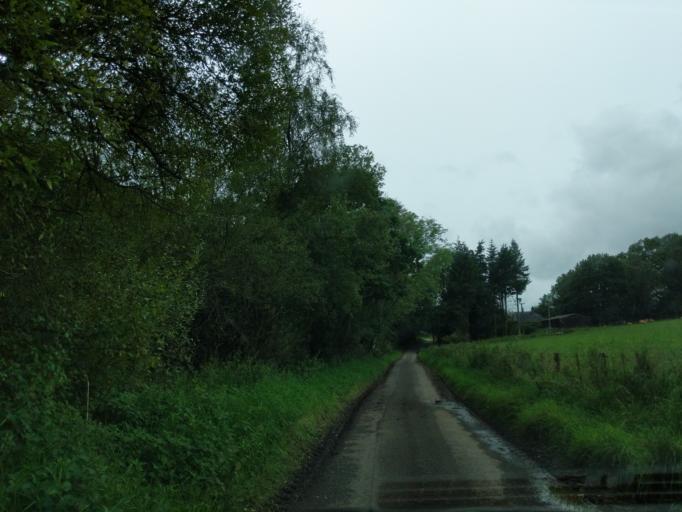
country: GB
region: Scotland
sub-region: The Scottish Borders
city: Galashiels
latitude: 55.5961
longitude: -2.7736
